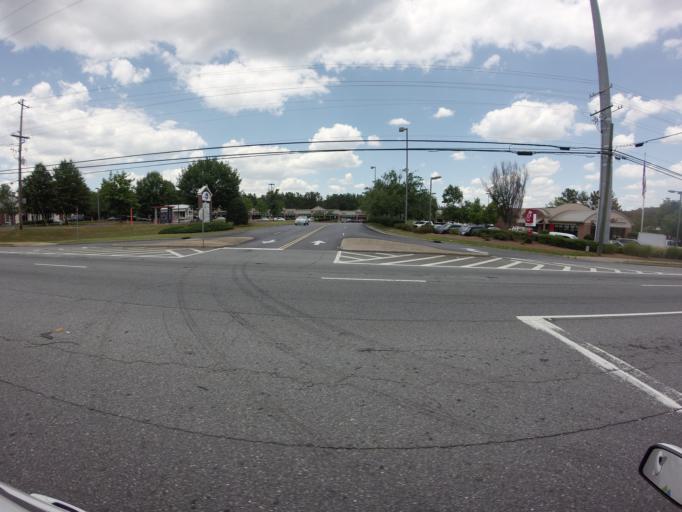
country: US
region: Georgia
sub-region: Gwinnett County
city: Norcross
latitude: 33.9865
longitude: -84.2712
